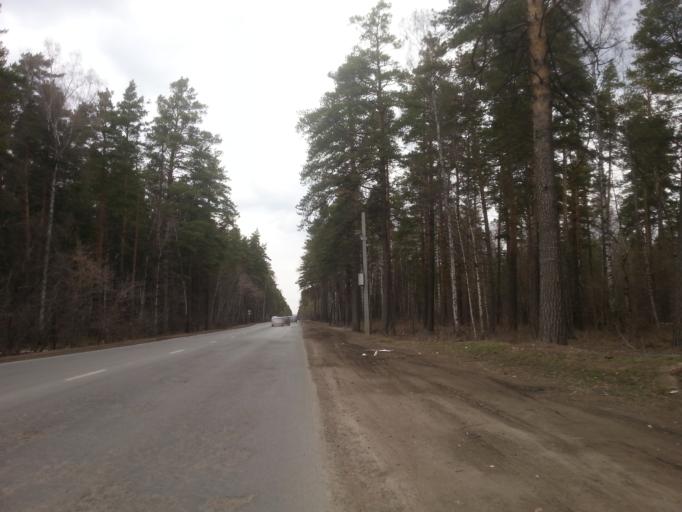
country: RU
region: Altai Krai
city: Yuzhnyy
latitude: 53.2718
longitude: 83.7237
